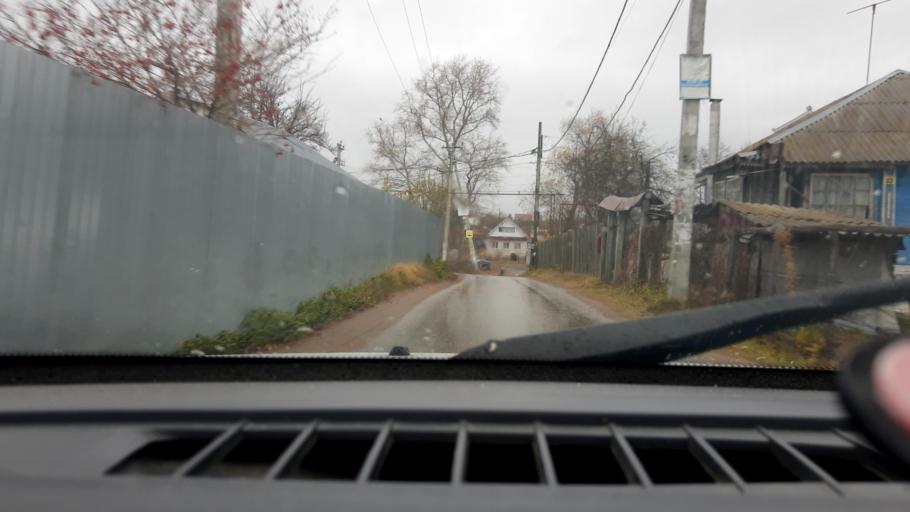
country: RU
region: Nizjnij Novgorod
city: Gorbatovka
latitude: 56.3807
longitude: 43.8157
